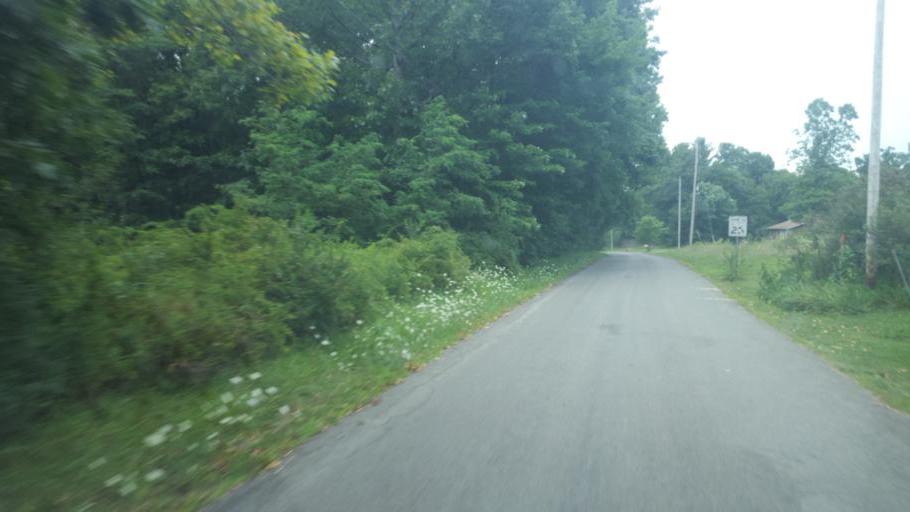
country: US
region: Pennsylvania
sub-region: Clarion County
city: Marianne
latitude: 41.2106
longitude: -79.4276
